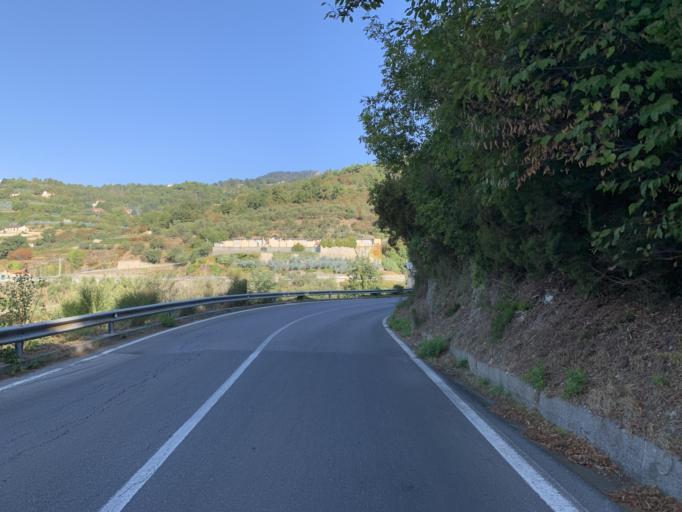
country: IT
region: Liguria
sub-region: Provincia di Savona
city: Magliolo
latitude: 44.1912
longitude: 8.2574
